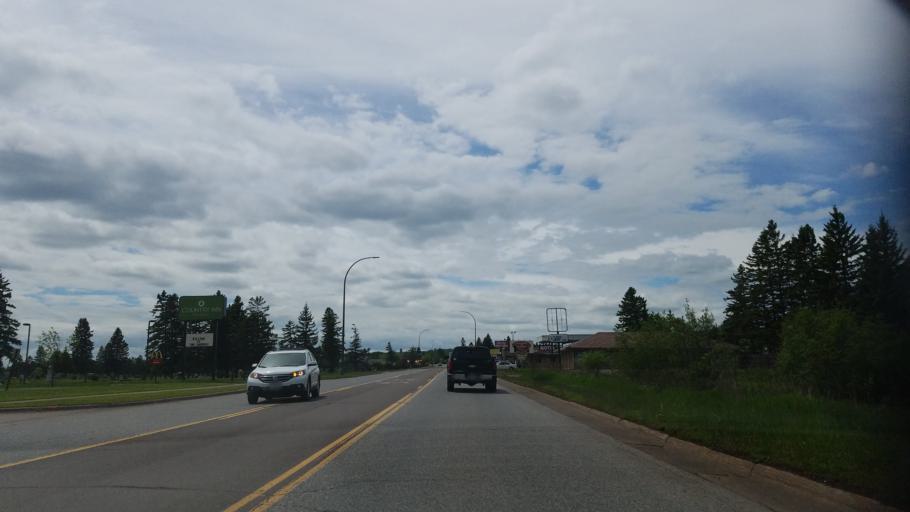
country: US
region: Minnesota
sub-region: Lake County
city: Two Harbors
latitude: 47.0256
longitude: -91.6815
